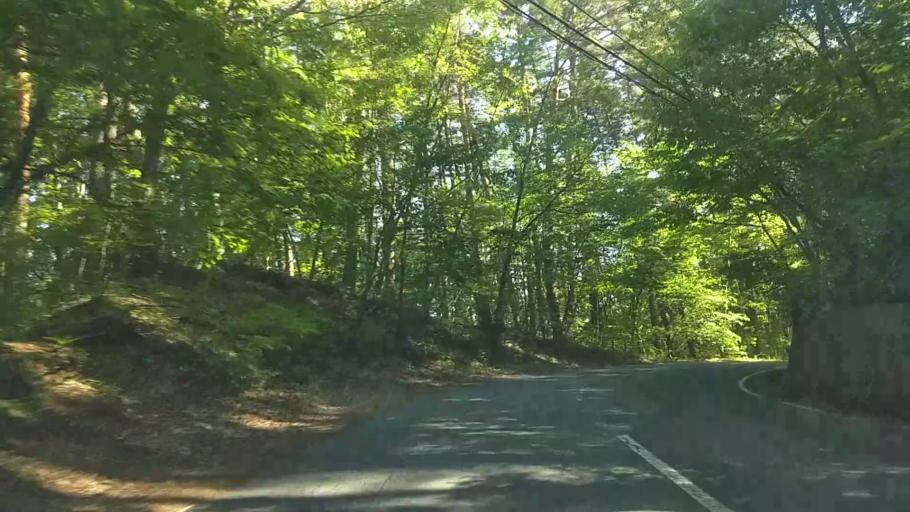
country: JP
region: Yamanashi
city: Nirasaki
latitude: 35.8901
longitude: 138.3923
